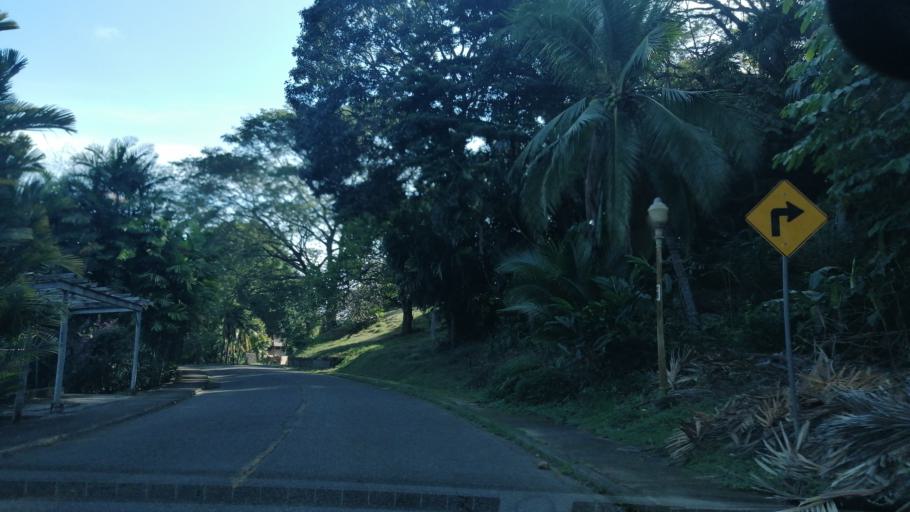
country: PA
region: Panama
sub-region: Distrito de Panama
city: Ancon
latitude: 8.9638
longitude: -79.5497
